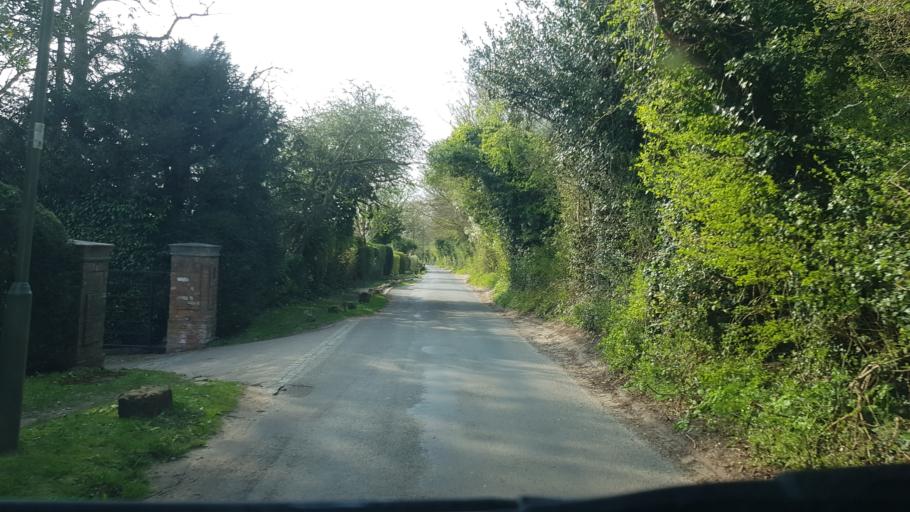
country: GB
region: England
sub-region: Surrey
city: Chilworth
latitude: 51.2319
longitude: -0.5337
